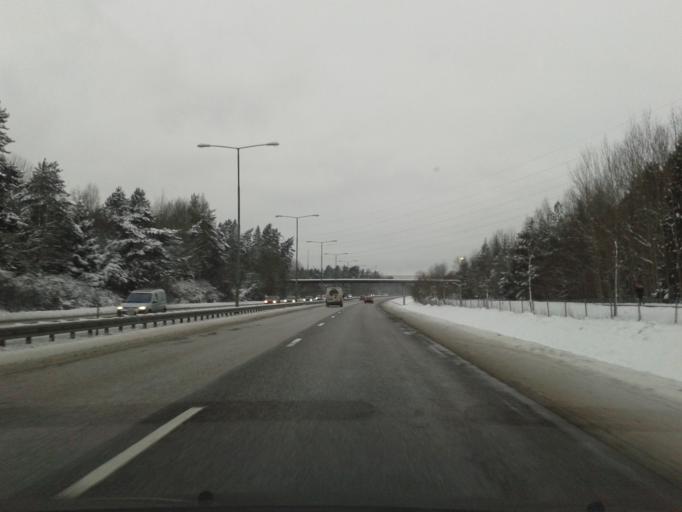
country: SE
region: Stockholm
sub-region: Stockholms Kommun
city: Arsta
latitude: 59.2590
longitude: 18.0755
